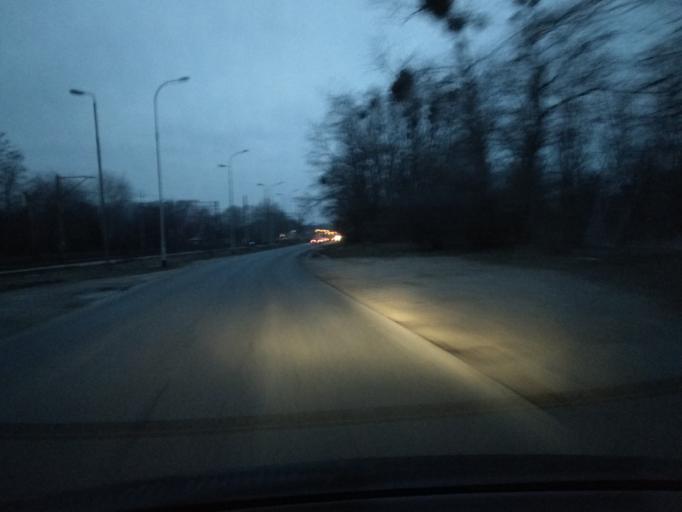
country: PL
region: Lower Silesian Voivodeship
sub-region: Powiat wroclawski
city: Wroclaw
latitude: 51.1244
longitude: 16.9576
